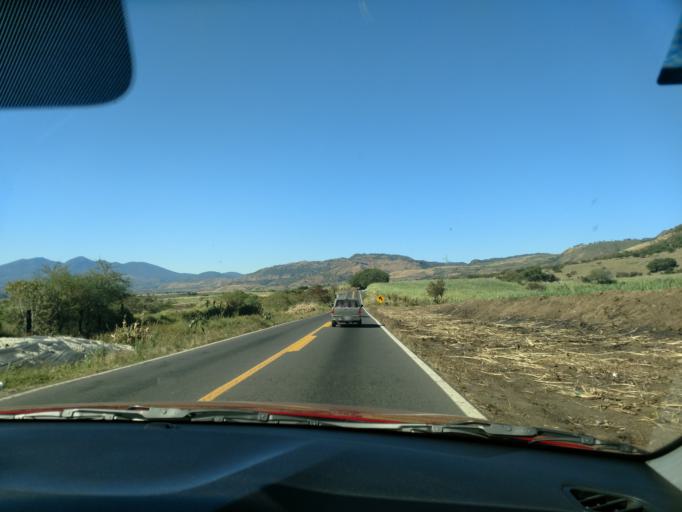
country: MX
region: Nayarit
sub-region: Ahuacatlan
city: Ahuacatlan
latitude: 21.1462
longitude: -104.6090
